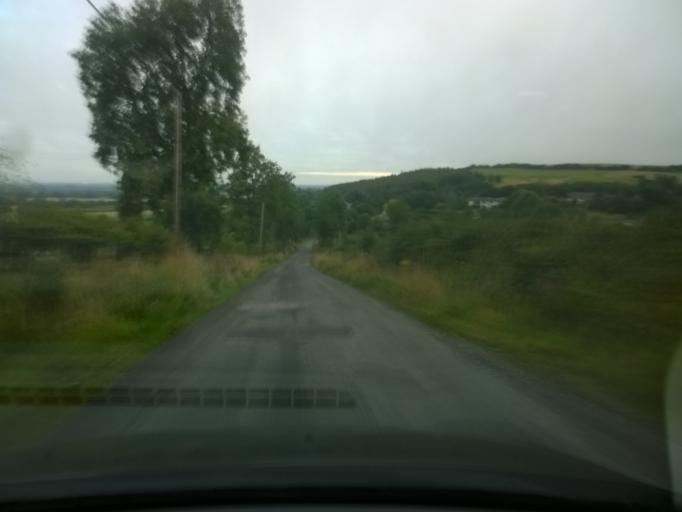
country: IE
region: Leinster
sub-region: Kildare
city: Cherryville
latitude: 53.1855
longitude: -6.9465
